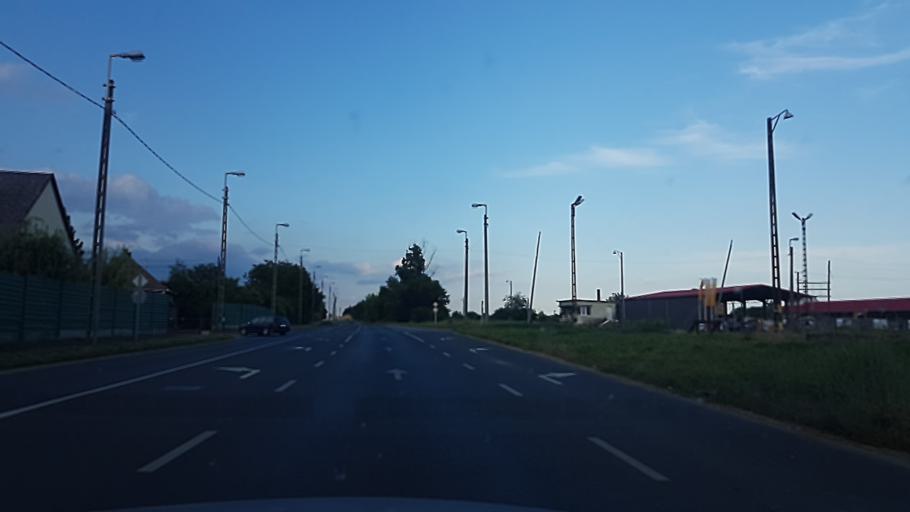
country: HU
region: Baranya
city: Szigetvar
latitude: 46.0431
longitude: 17.8076
